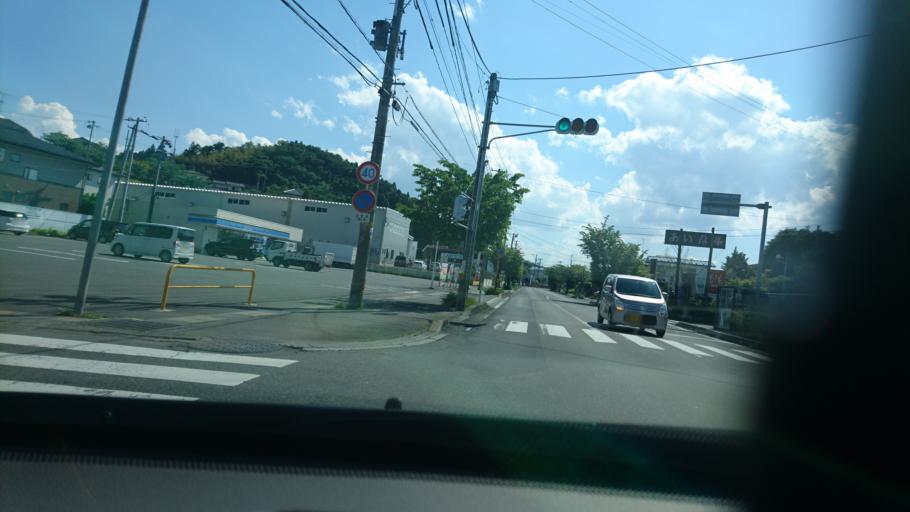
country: JP
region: Iwate
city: Ichinoseki
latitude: 38.9304
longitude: 141.1580
